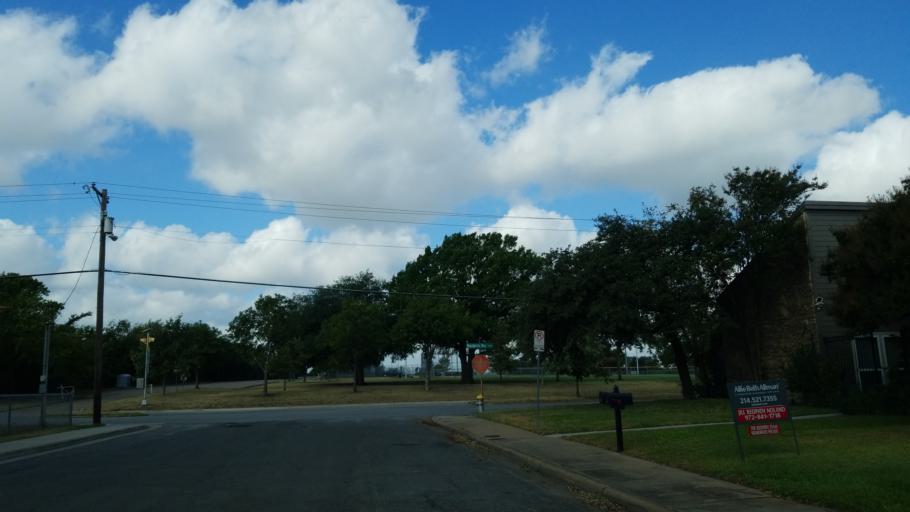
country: US
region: Texas
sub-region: Dallas County
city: Richardson
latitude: 32.9484
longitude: -96.7782
